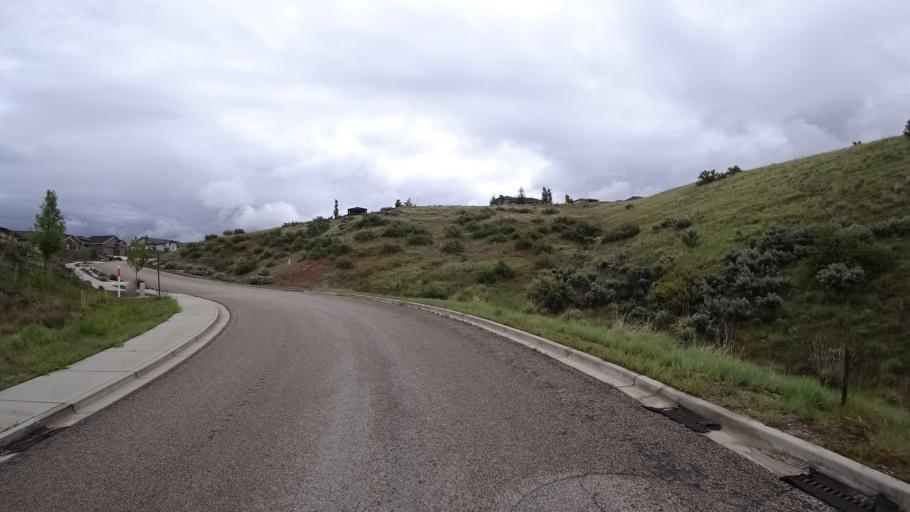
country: US
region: Idaho
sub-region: Ada County
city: Eagle
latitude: 43.7712
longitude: -116.2583
